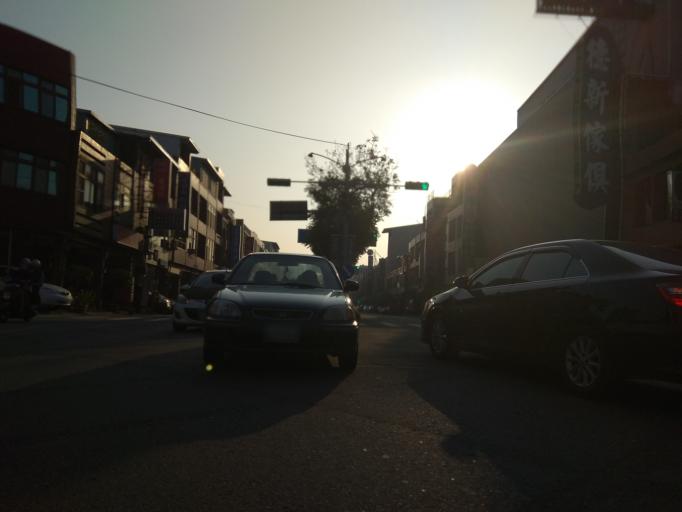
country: TW
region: Taiwan
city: Daxi
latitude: 24.9221
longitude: 121.1867
